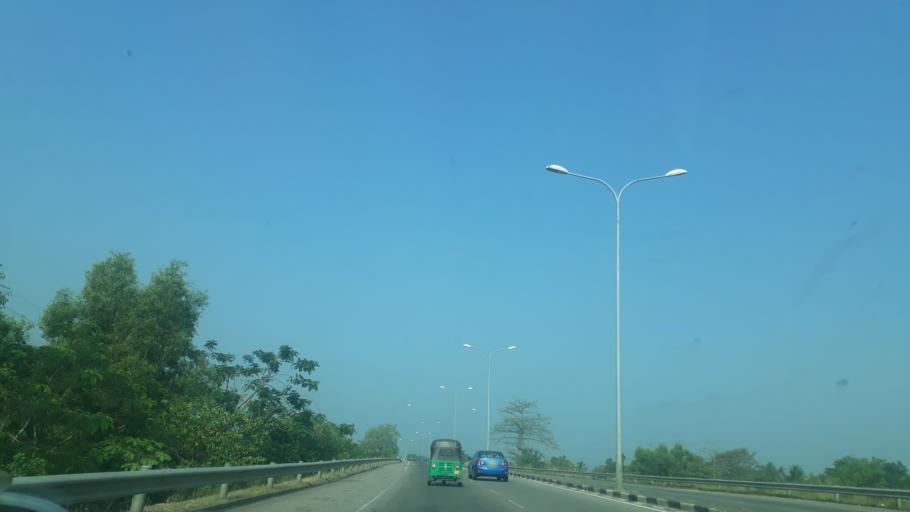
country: LK
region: Western
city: Wattala
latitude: 6.9686
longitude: 79.8996
